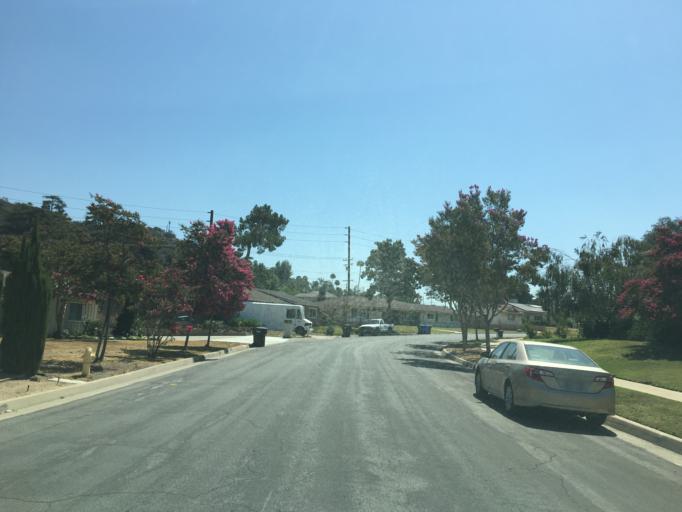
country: US
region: California
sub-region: Los Angeles County
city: La Verne
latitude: 34.1211
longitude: -117.7583
